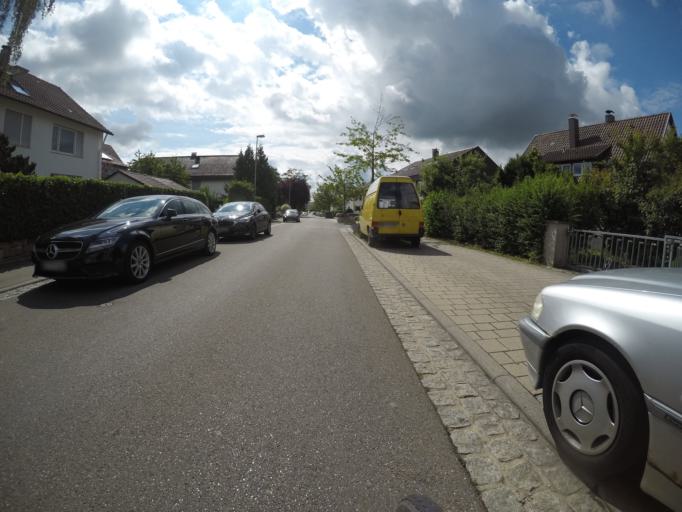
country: DE
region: Baden-Wuerttemberg
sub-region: Regierungsbezirk Stuttgart
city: Ostfildern
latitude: 48.7297
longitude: 9.2560
